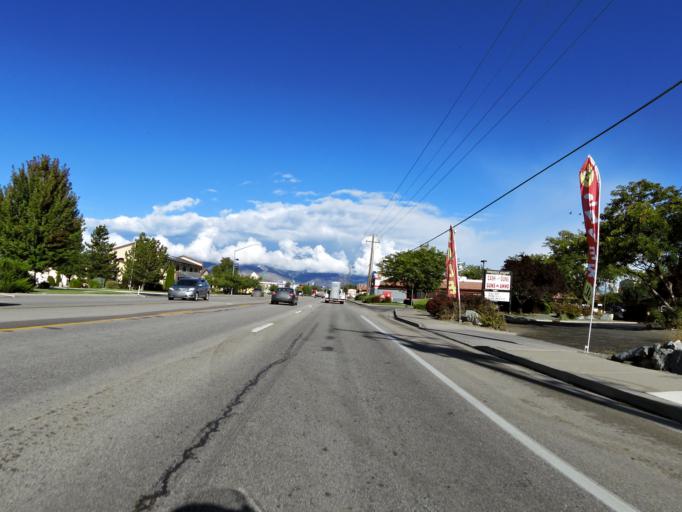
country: US
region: Nevada
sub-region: Douglas County
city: Gardnerville
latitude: 38.9345
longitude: -119.7369
